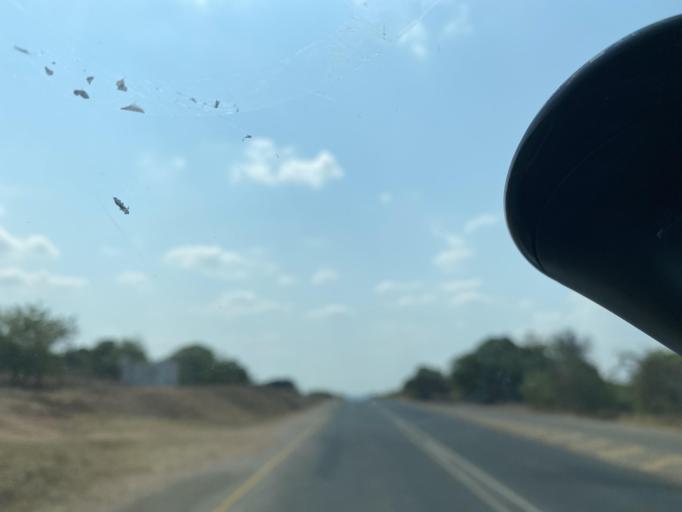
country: ZM
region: Lusaka
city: Chongwe
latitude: -15.5944
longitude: 28.7174
